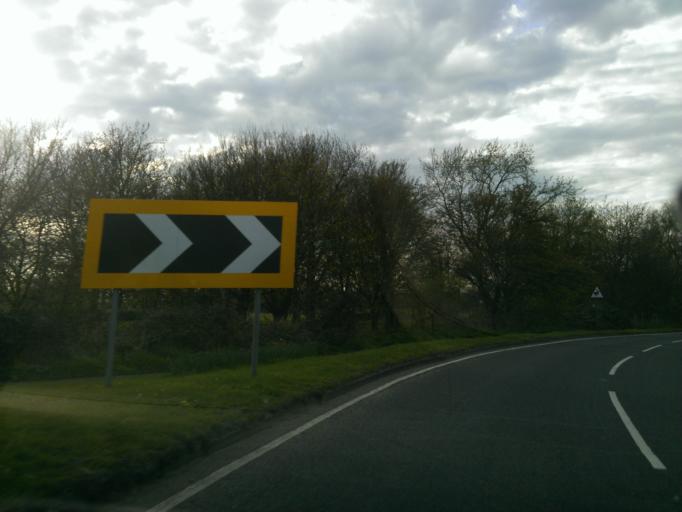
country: GB
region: England
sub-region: Essex
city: Saint Osyth
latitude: 51.8053
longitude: 1.0789
